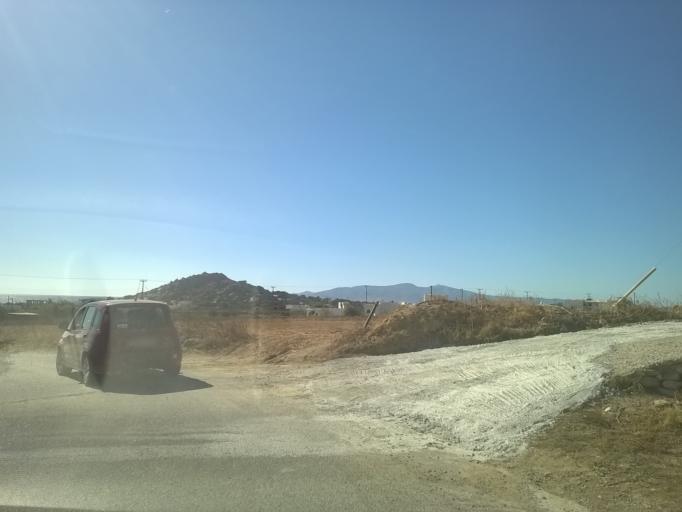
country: GR
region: South Aegean
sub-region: Nomos Kykladon
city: Naxos
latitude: 37.0247
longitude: 25.3786
